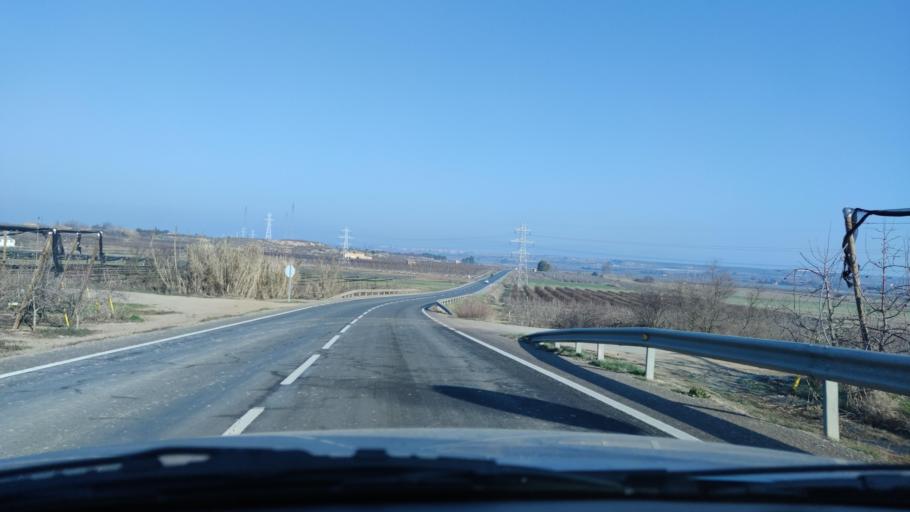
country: ES
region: Catalonia
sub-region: Provincia de Lleida
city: Torrefarrera
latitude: 41.7031
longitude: 0.6368
